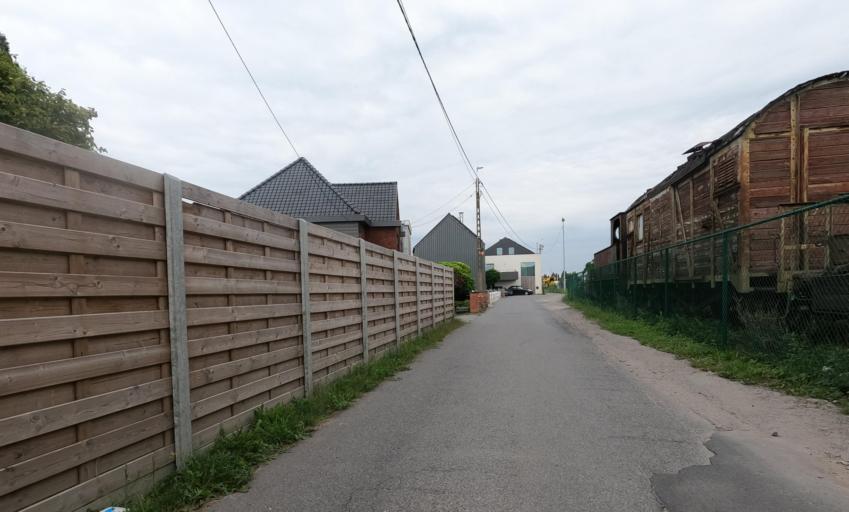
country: BE
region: Flanders
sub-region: Provincie Oost-Vlaanderen
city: Buggenhout
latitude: 51.0285
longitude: 4.1755
